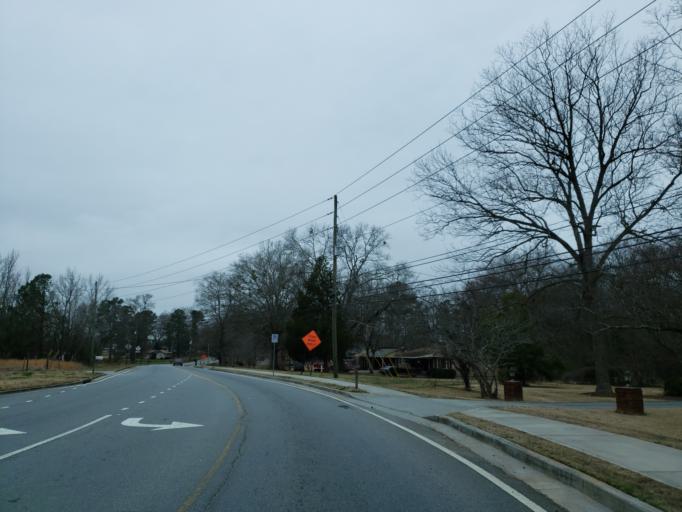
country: US
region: Georgia
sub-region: Cobb County
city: Marietta
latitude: 33.9299
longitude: -84.6334
